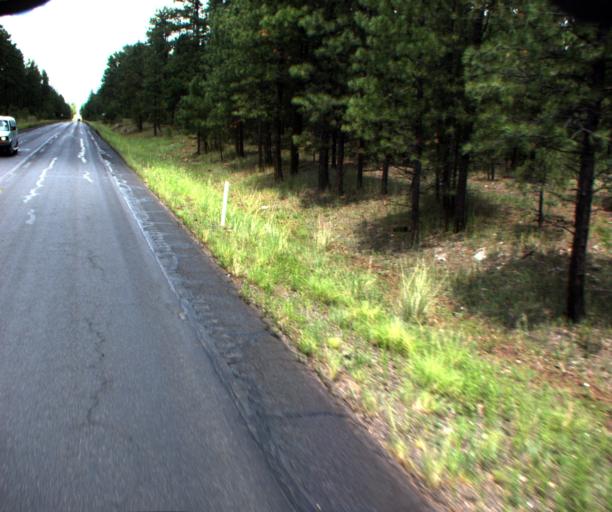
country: US
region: Arizona
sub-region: Gila County
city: Pine
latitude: 34.4691
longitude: -111.4482
